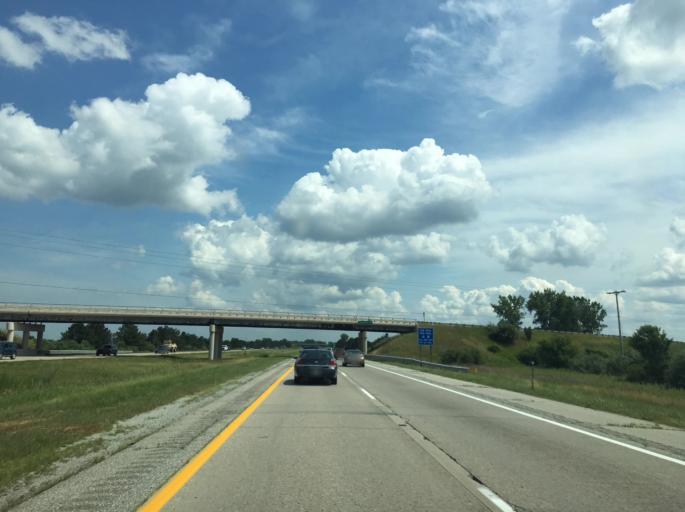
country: US
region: Michigan
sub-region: Bay County
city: Auburn
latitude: 43.6518
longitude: -83.9911
